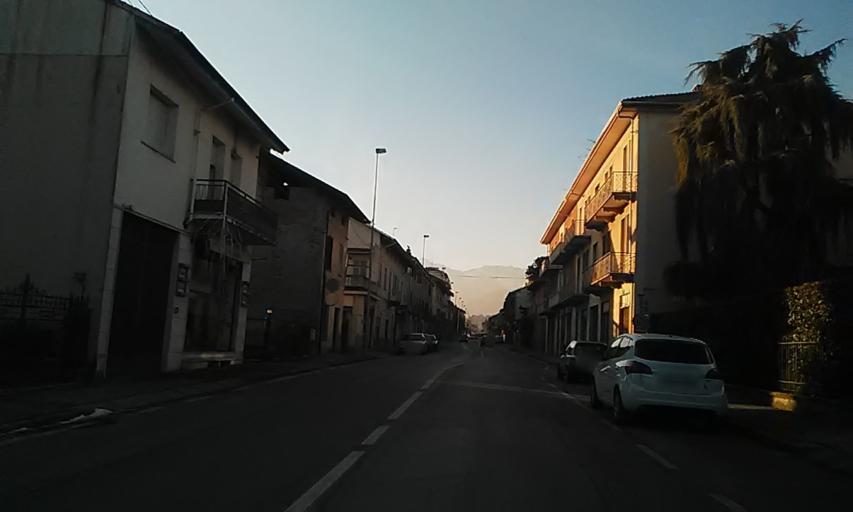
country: IT
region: Piedmont
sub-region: Provincia di Biella
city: Vigliano Biellese
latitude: 45.5643
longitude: 8.0993
